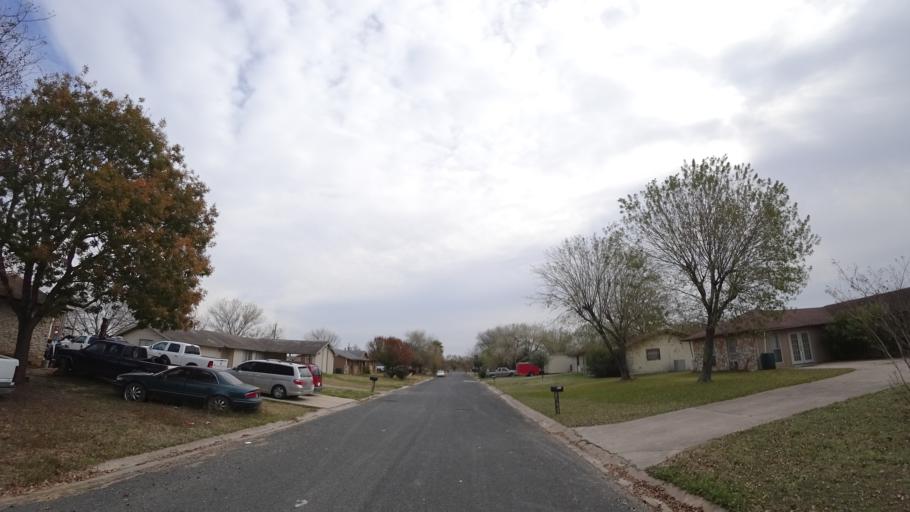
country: US
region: Texas
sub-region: Travis County
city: Onion Creek
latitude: 30.1367
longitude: -97.6779
